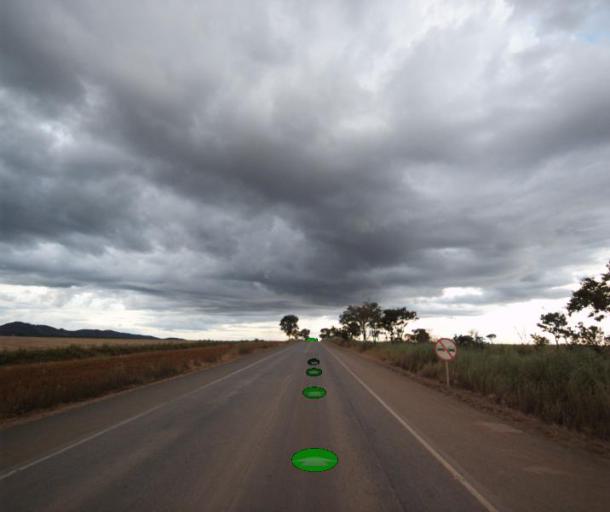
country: BR
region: Goias
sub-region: Uruacu
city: Uruacu
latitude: -14.7101
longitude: -49.2249
